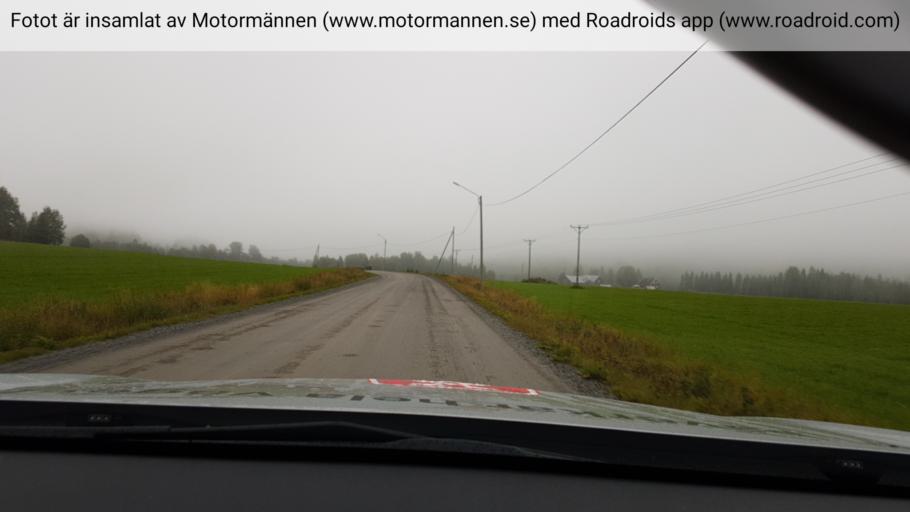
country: SE
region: Vaesterbotten
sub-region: Vannas Kommun
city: Vannasby
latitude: 64.1020
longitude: 19.9862
